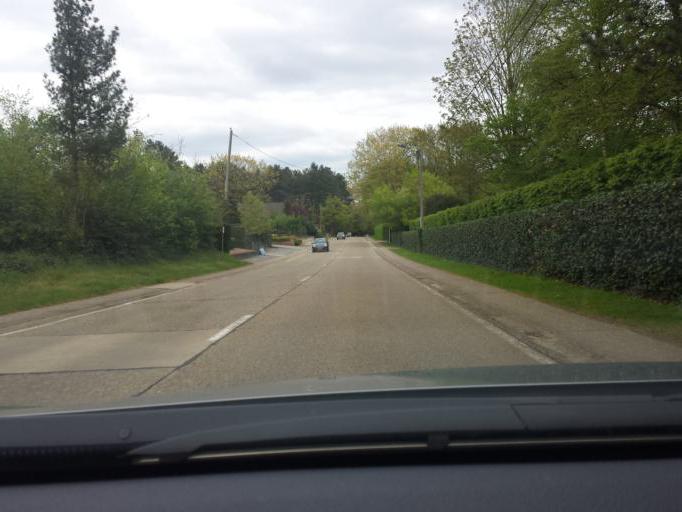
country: BE
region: Flanders
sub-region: Provincie Limburg
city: Lummen
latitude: 50.9892
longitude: 5.2058
